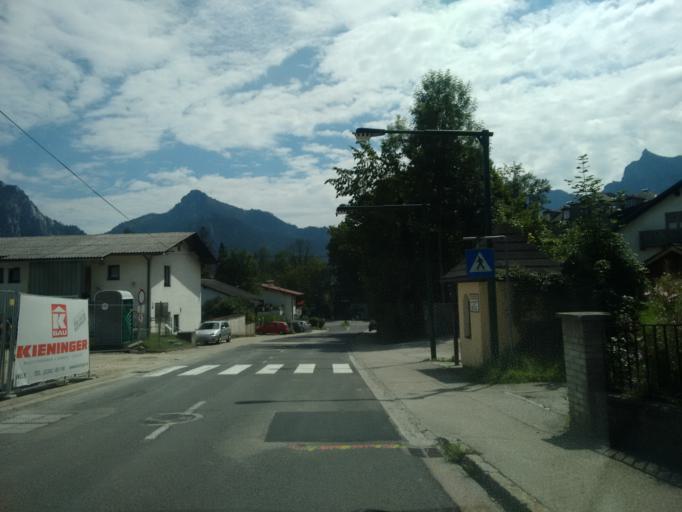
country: AT
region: Upper Austria
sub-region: Politischer Bezirk Gmunden
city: Ebensee
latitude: 47.8535
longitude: 13.7767
